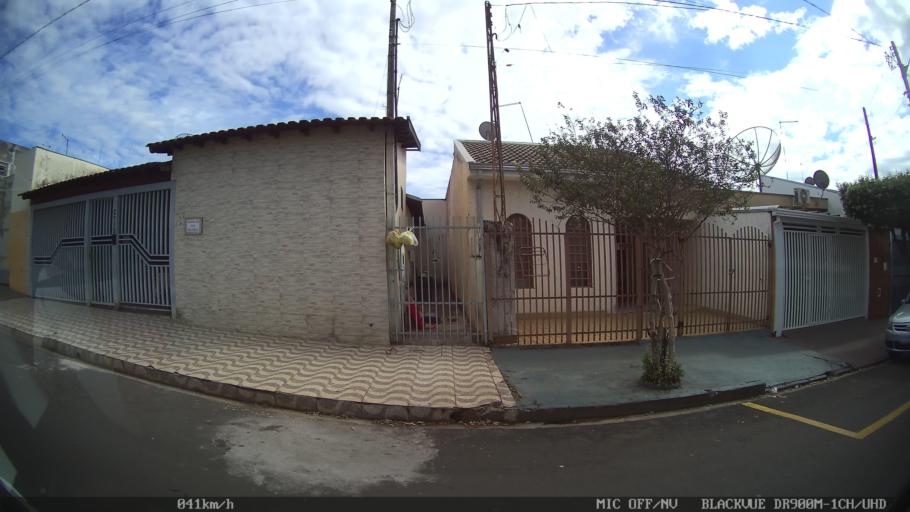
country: BR
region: Sao Paulo
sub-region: Bady Bassitt
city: Bady Bassitt
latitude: -20.8116
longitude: -49.5158
